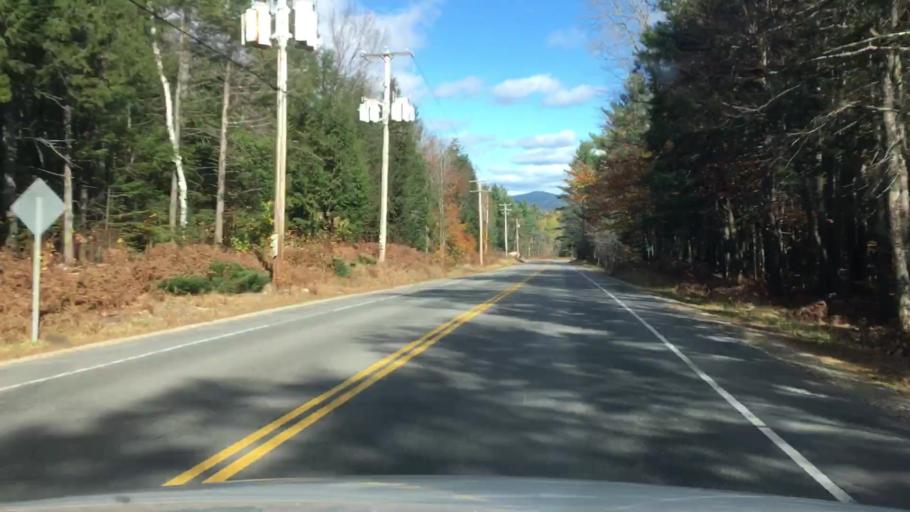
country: US
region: New Hampshire
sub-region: Coos County
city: Gorham
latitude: 44.3517
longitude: -71.1938
